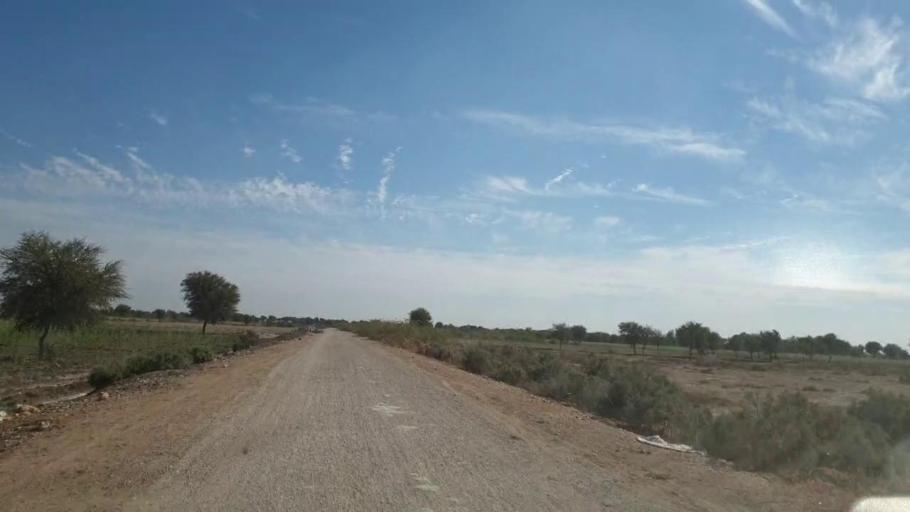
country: PK
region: Sindh
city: Pithoro
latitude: 25.5542
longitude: 69.2981
